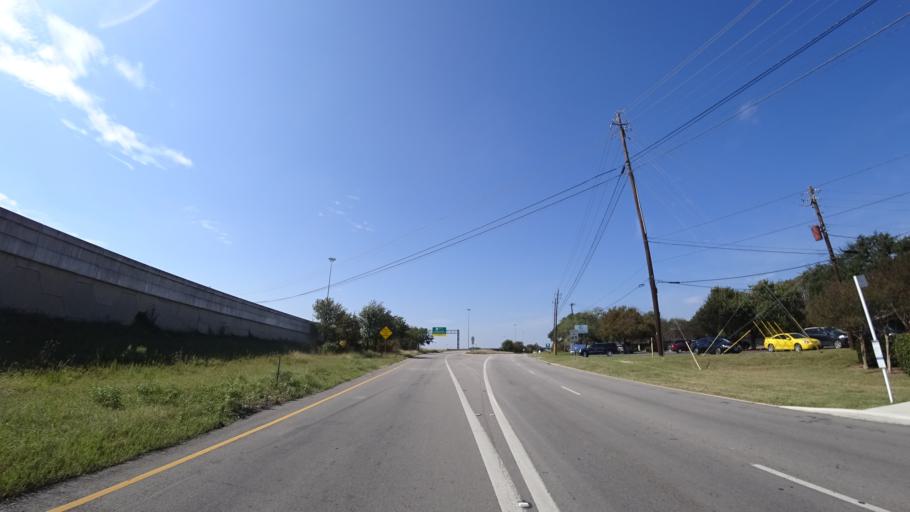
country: US
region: Texas
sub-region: Travis County
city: Rollingwood
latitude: 30.2322
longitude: -97.8044
